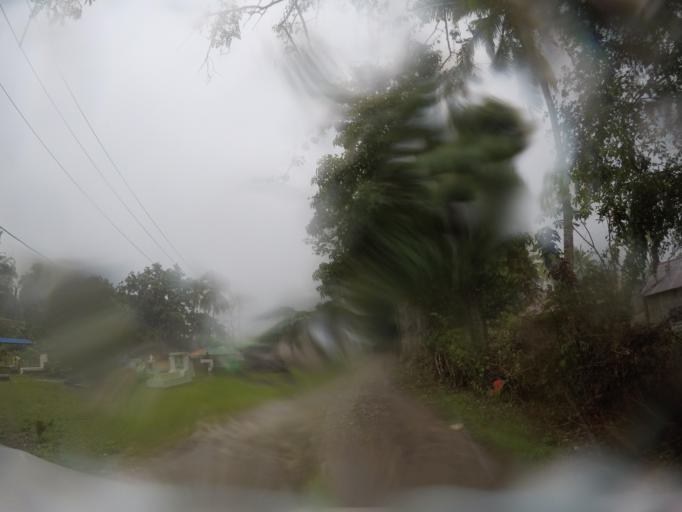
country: TL
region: Baucau
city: Venilale
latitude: -8.6337
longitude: 126.4415
